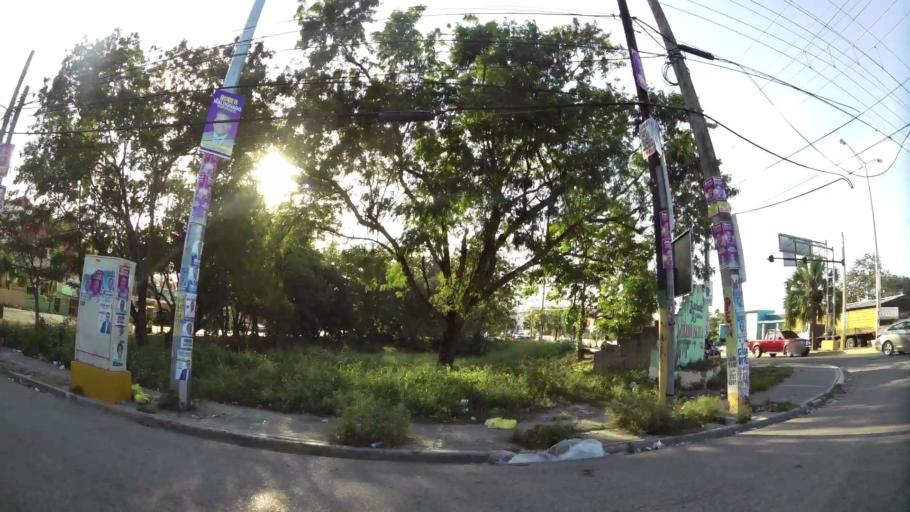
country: DO
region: Nacional
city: Ensanche Luperon
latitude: 18.5468
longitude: -69.9049
